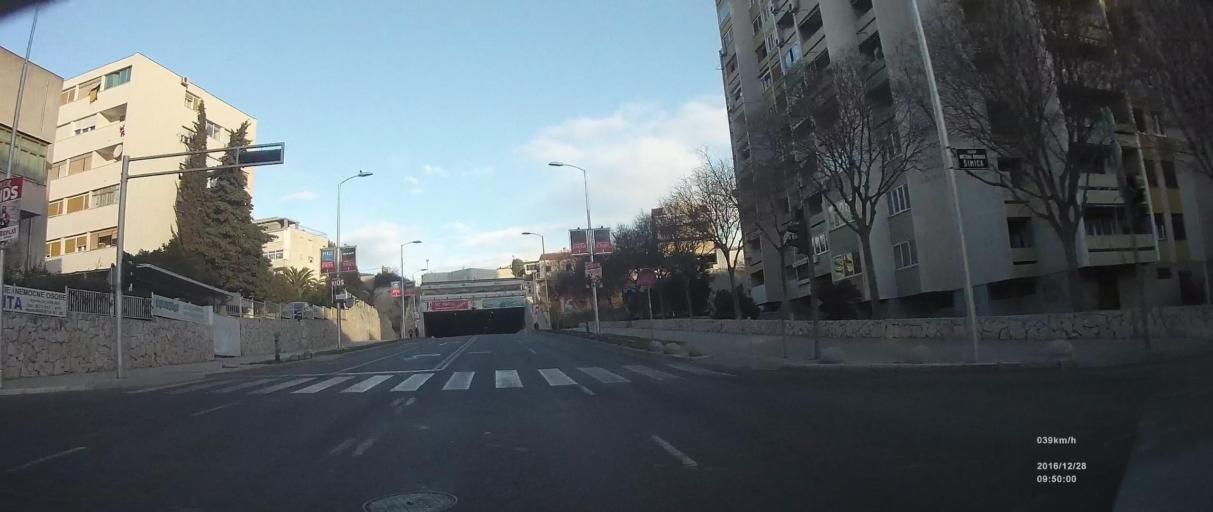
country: HR
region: Splitsko-Dalmatinska
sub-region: Grad Split
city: Split
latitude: 43.5065
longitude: 16.4560
